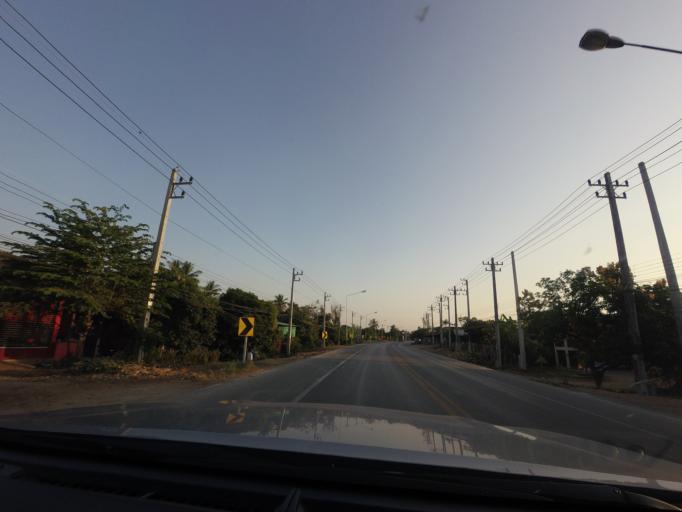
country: TH
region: Sukhothai
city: Si Samrong
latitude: 17.2083
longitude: 99.8680
